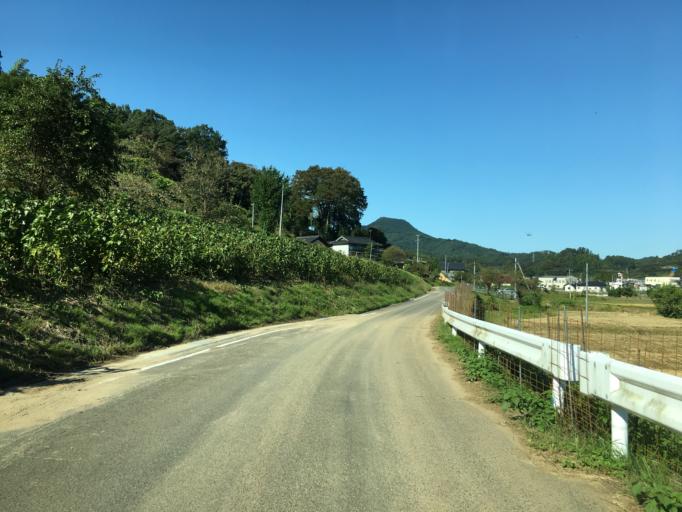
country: JP
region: Fukushima
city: Fukushima-shi
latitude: 37.6783
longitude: 140.5628
